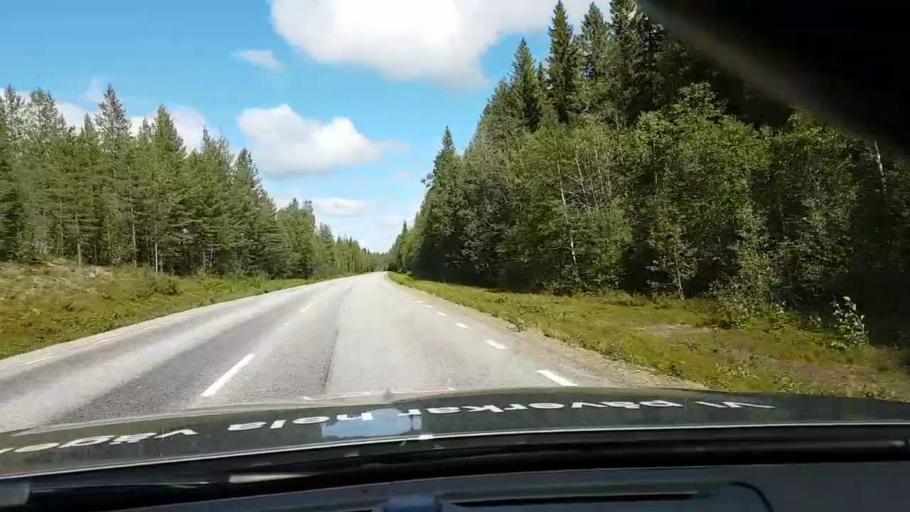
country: SE
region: Vaesternorrland
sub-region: OErnskoeldsviks Kommun
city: Bredbyn
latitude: 63.6246
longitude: 17.9077
